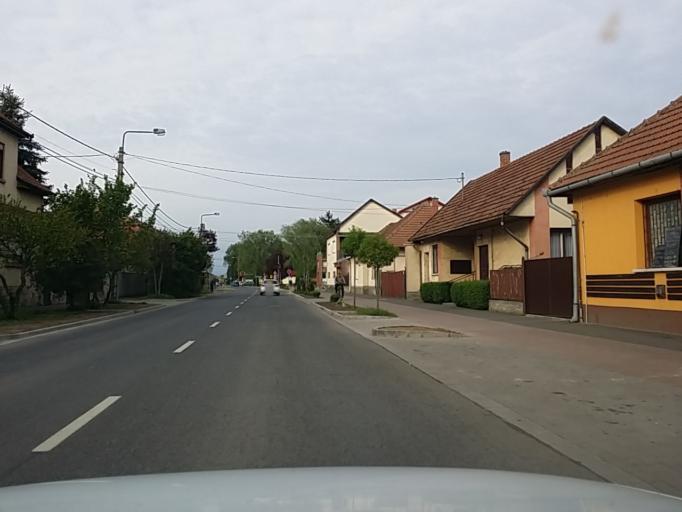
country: HU
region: Heves
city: Boldog
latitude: 47.5704
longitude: 19.7176
